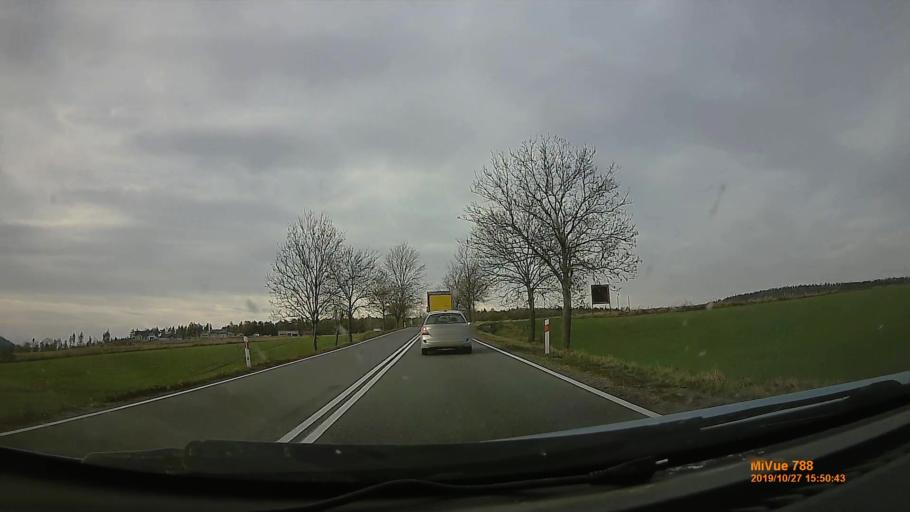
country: PL
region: Lower Silesian Voivodeship
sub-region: Powiat klodzki
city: Bozkow
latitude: 50.5199
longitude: 16.5843
